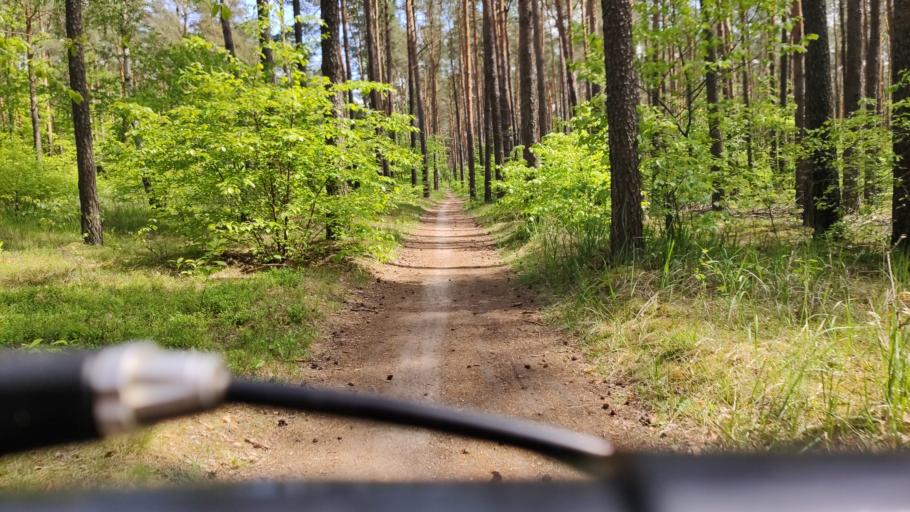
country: PL
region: Kujawsko-Pomorskie
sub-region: Wloclawek
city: Wloclawek
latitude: 52.6334
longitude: 19.1299
